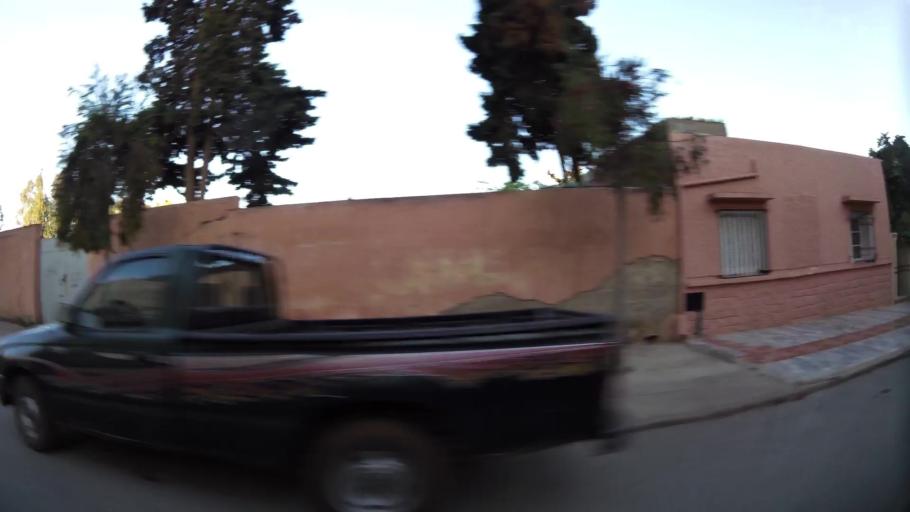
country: MA
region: Oriental
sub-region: Berkane-Taourirt
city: Berkane
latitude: 34.9246
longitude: -2.3273
